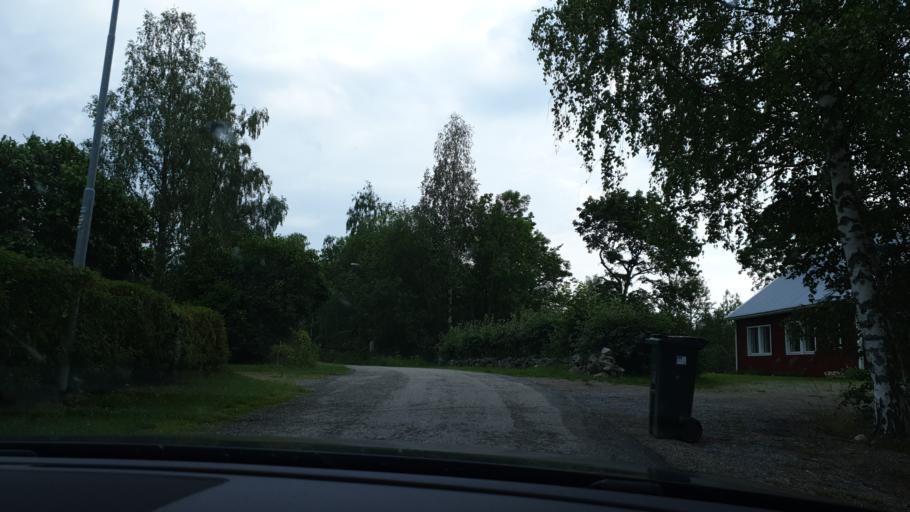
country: SE
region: Gaevleborg
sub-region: Hudiksvalls Kommun
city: Iggesund
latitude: 61.5418
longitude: 17.0057
